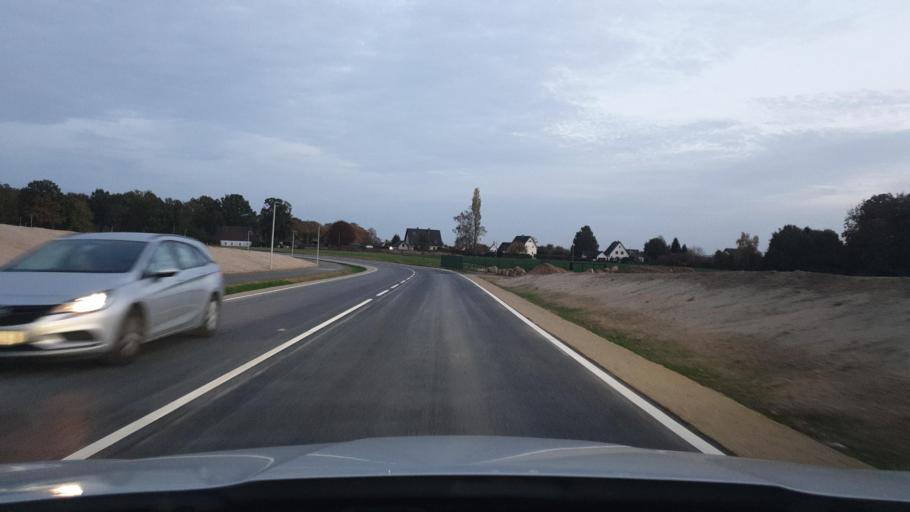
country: DE
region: North Rhine-Westphalia
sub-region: Regierungsbezirk Detmold
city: Bielefeld
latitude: 52.0668
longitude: 8.5743
